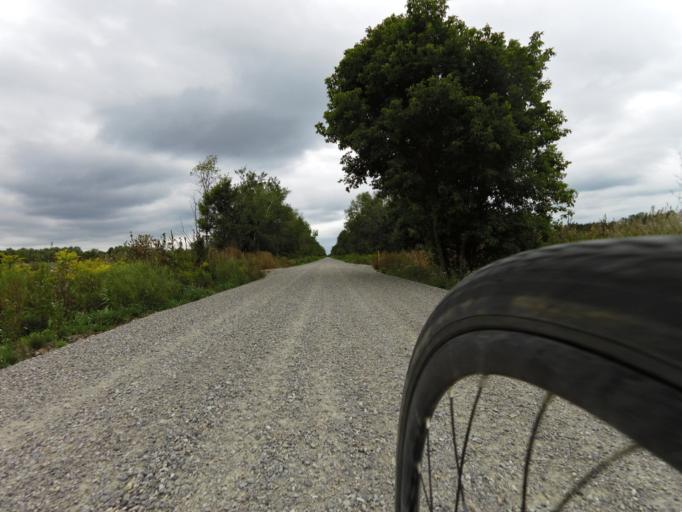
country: CA
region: Ontario
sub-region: Lanark County
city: Smiths Falls
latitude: 44.9316
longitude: -76.0348
